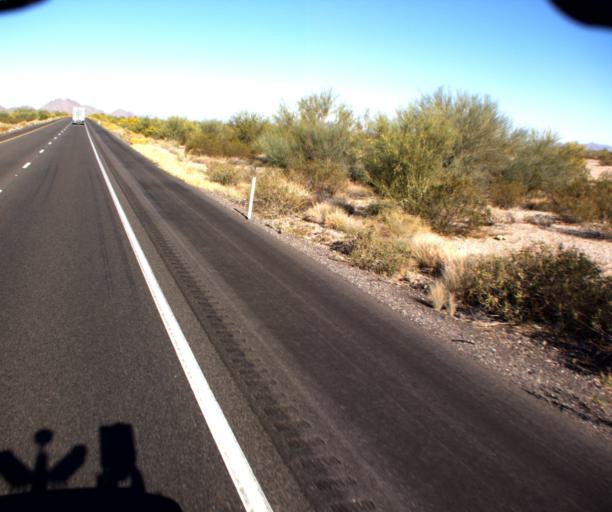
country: US
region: Arizona
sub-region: Maricopa County
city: Gila Bend
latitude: 32.8860
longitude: -112.4695
